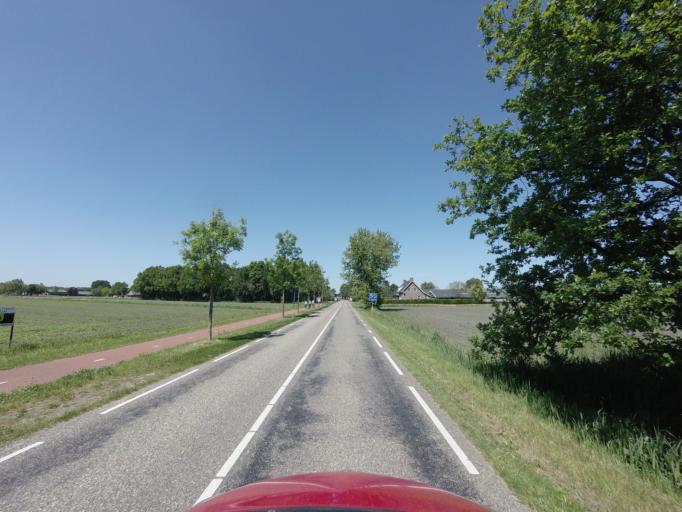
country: BE
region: Flanders
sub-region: Provincie Limburg
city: Lommel
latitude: 51.2812
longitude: 5.3157
